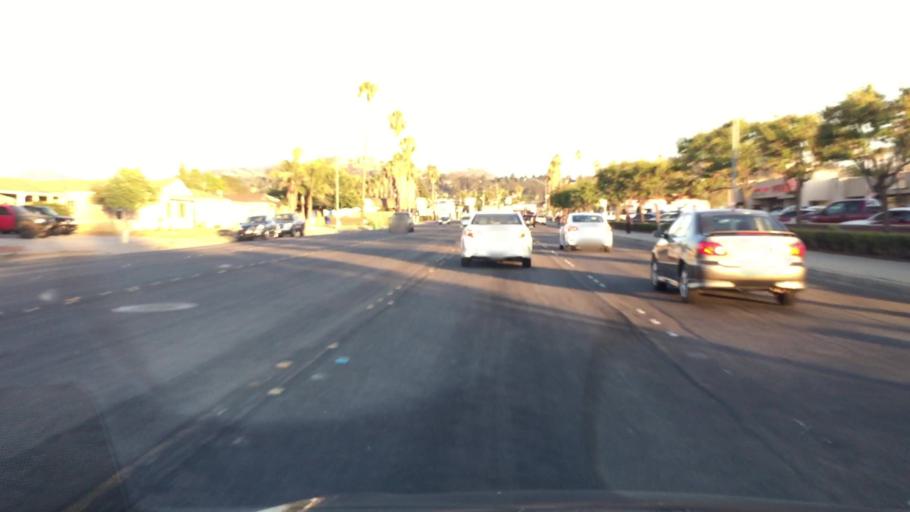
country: US
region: California
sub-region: San Diego County
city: Bostonia
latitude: 32.7897
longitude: -116.9303
